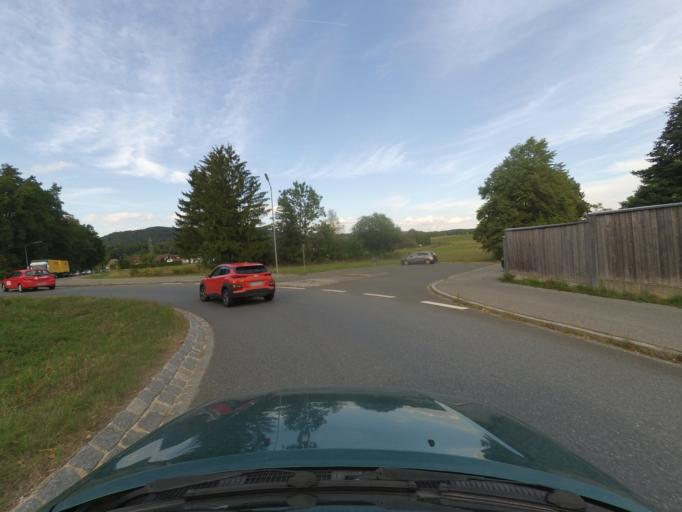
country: DE
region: Bavaria
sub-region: Regierungsbezirk Mittelfranken
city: Altdorf
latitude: 49.3944
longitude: 11.3497
